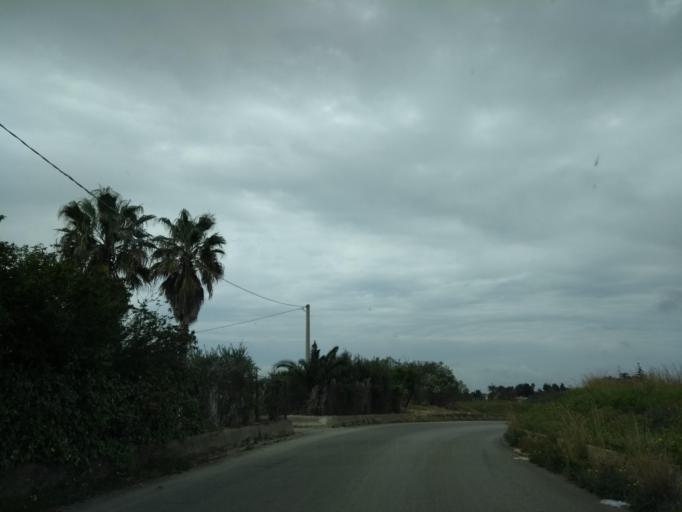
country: IT
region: Sicily
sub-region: Palermo
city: Partinico
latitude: 38.0087
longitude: 13.0674
